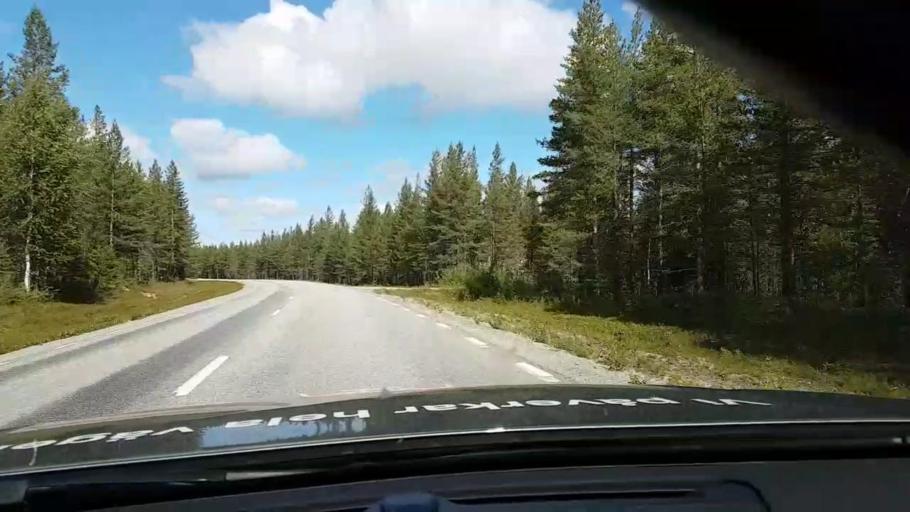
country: SE
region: Vaesternorrland
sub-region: OErnskoeldsviks Kommun
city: Bredbyn
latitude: 63.6157
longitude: 17.9064
